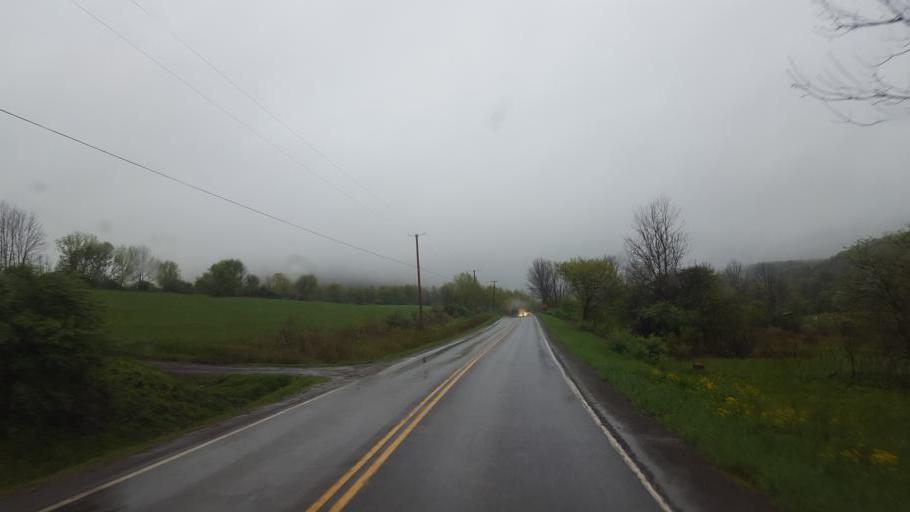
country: US
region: Pennsylvania
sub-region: Tioga County
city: Elkland
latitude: 42.0630
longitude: -77.4405
